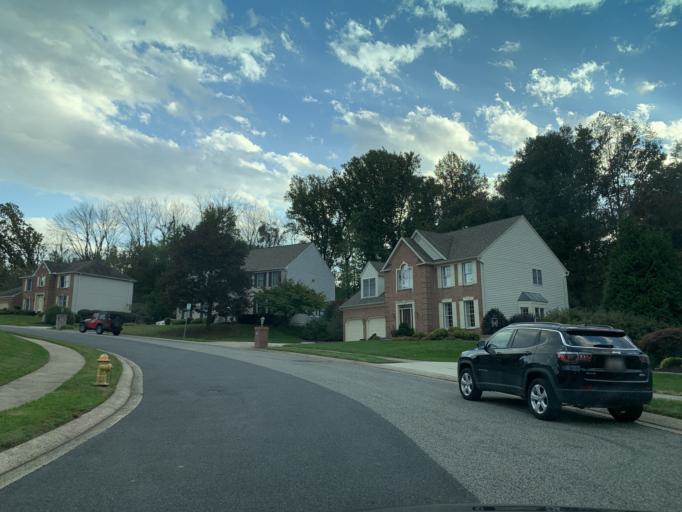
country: US
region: Maryland
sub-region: Harford County
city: Bel Air South
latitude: 39.5100
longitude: -76.3247
